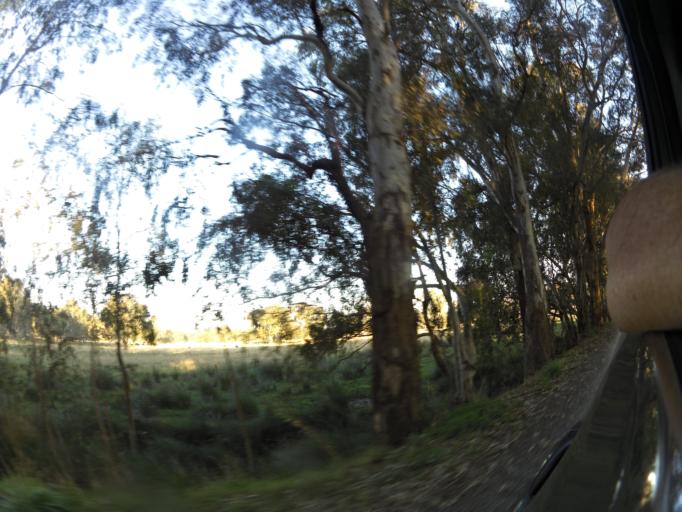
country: AU
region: Victoria
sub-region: Murrindindi
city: Alexandra
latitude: -37.1537
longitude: 145.5442
